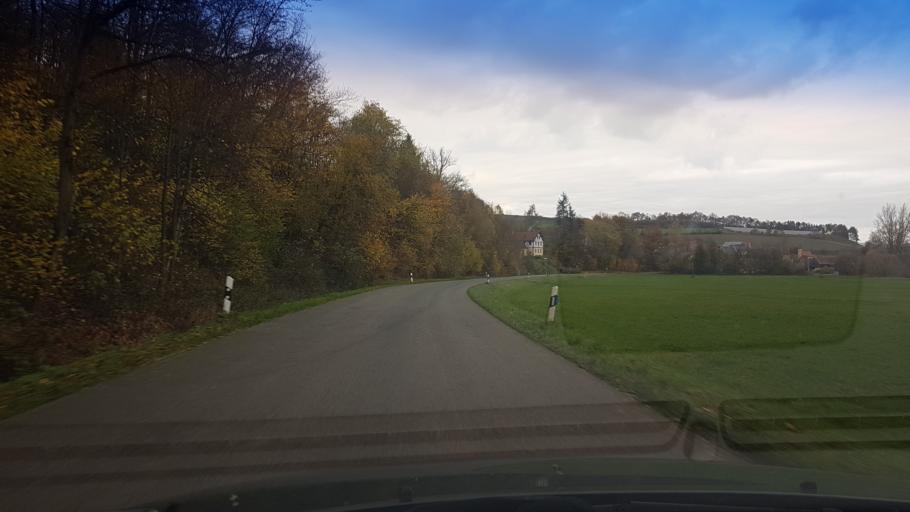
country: DE
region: Bavaria
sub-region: Upper Franconia
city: Rattelsdorf
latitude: 50.0435
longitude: 10.8736
